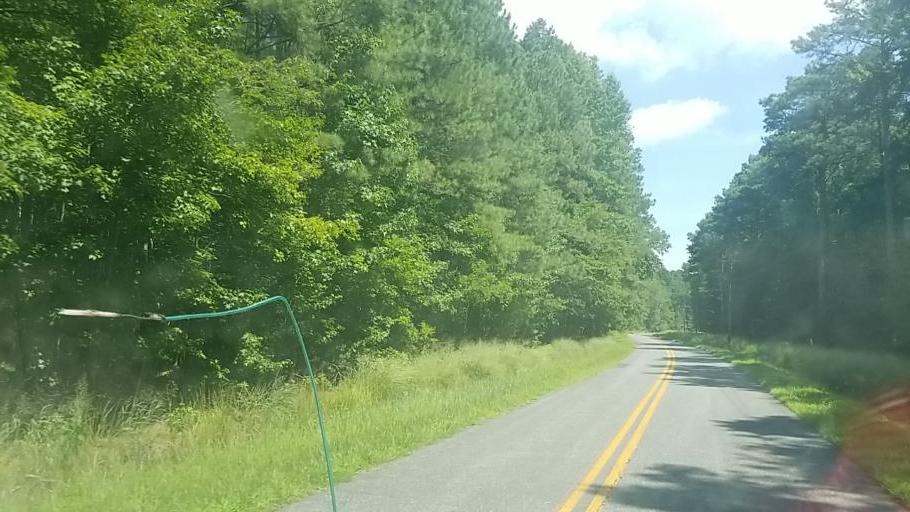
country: US
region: Maryland
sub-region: Wicomico County
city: Hebron
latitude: 38.4270
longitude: -75.8795
